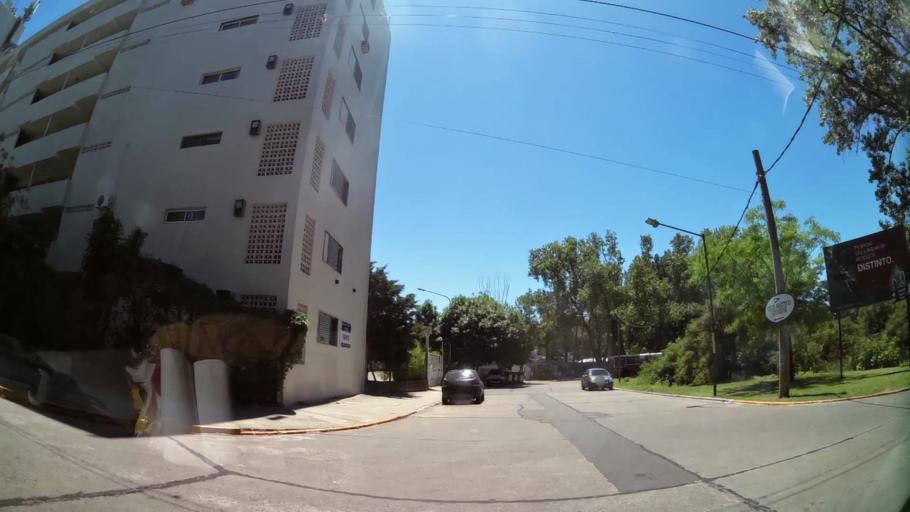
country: AR
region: Buenos Aires
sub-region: Partido de San Isidro
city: San Isidro
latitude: -34.4521
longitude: -58.5206
